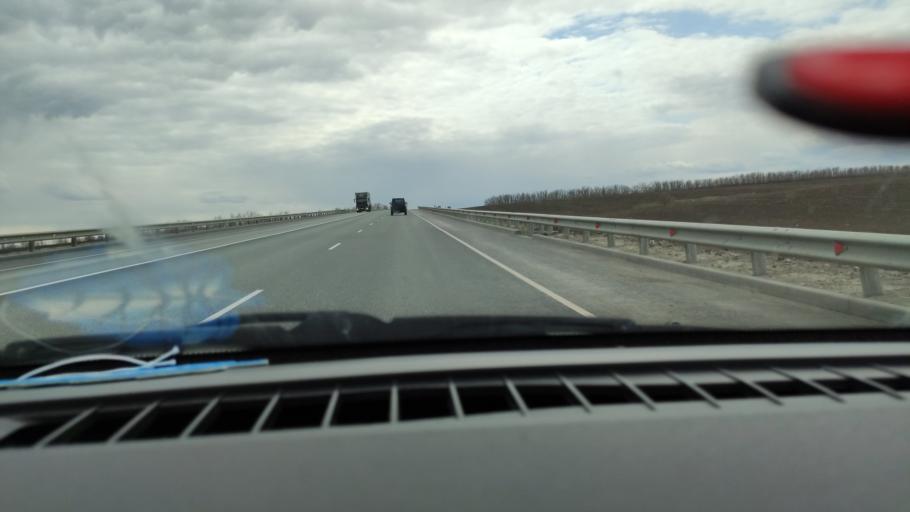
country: RU
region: Saratov
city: Yelshanka
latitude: 51.8354
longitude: 46.4700
